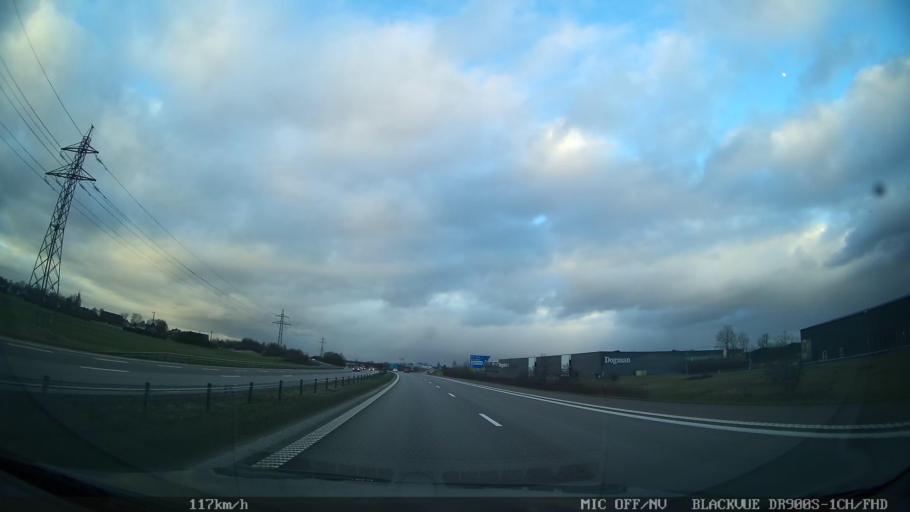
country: SE
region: Skane
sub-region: Astorps Kommun
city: Astorp
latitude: 56.1240
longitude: 12.9067
